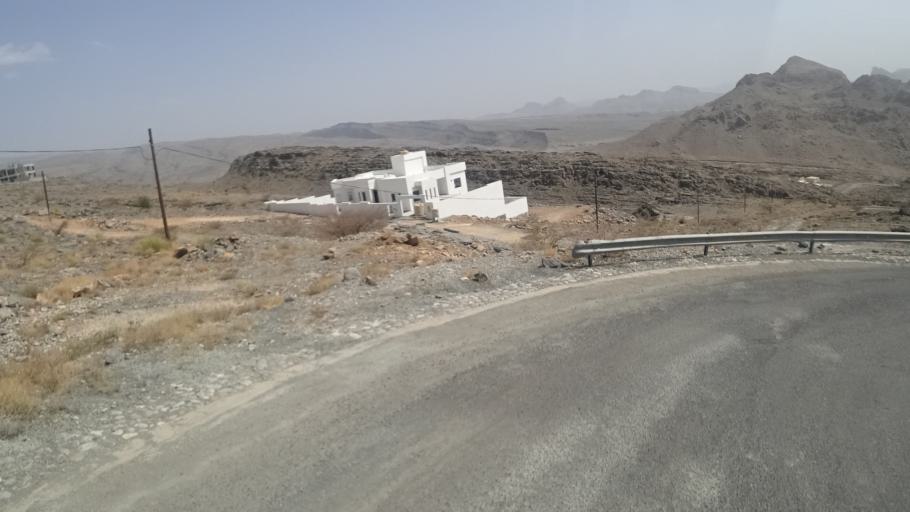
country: OM
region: Muhafazat ad Dakhiliyah
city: Bahla'
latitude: 23.1336
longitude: 57.3057
